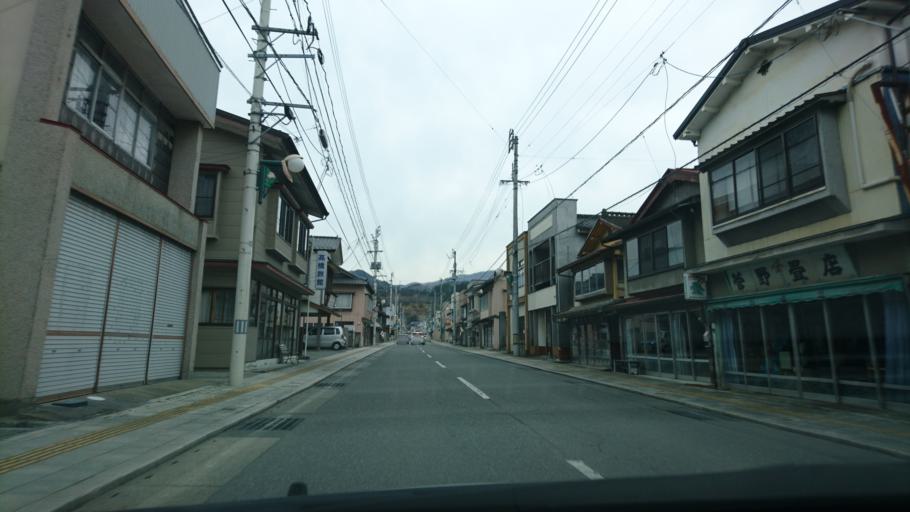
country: JP
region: Iwate
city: Ofunato
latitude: 39.1389
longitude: 141.5781
